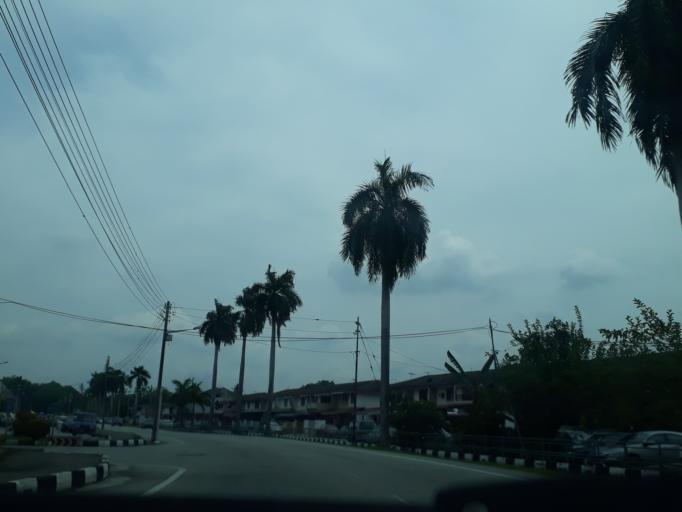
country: MY
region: Perak
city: Ipoh
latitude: 4.5956
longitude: 101.1274
